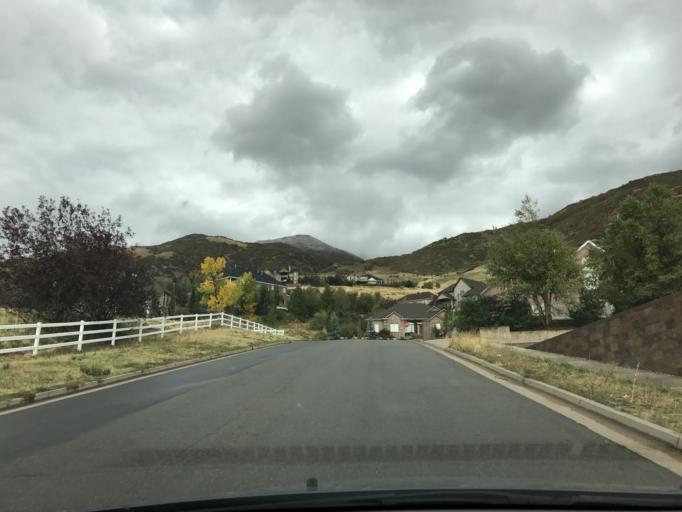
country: US
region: Utah
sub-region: Davis County
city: Fruit Heights
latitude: 41.0084
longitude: -111.8970
